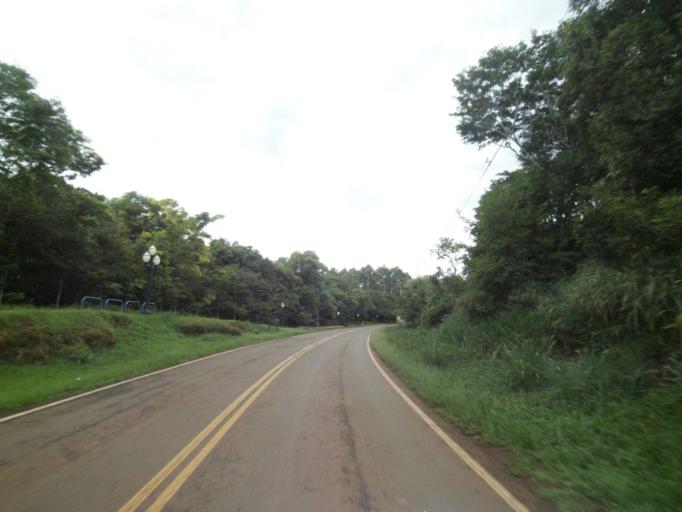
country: BR
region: Parana
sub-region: Guaraniacu
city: Guaraniacu
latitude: -25.0974
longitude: -52.8858
